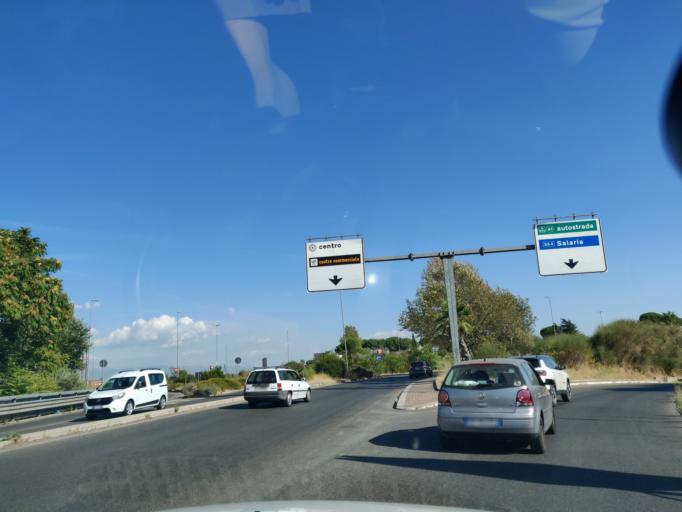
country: IT
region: Latium
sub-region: Citta metropolitana di Roma Capitale
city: Colle Verde
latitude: 41.9688
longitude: 12.5387
